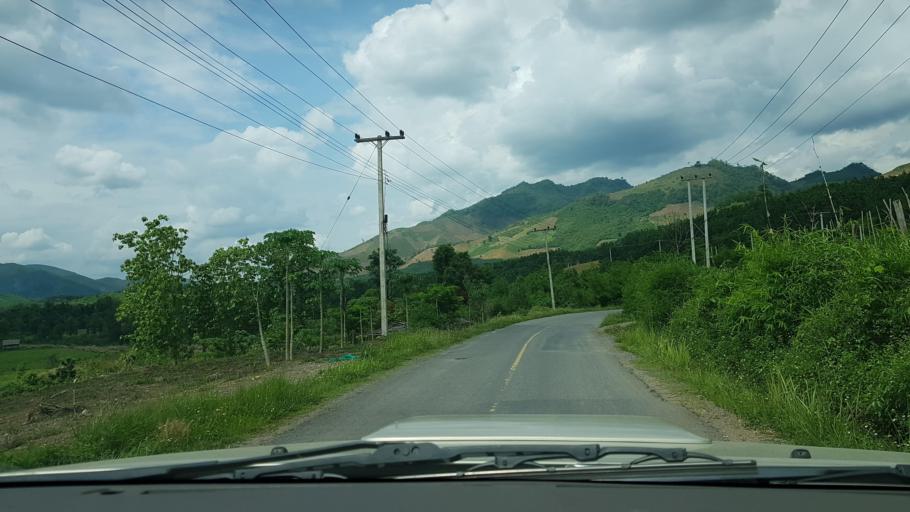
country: LA
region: Loungnamtha
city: Muang Nale
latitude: 20.1774
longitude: 101.5162
